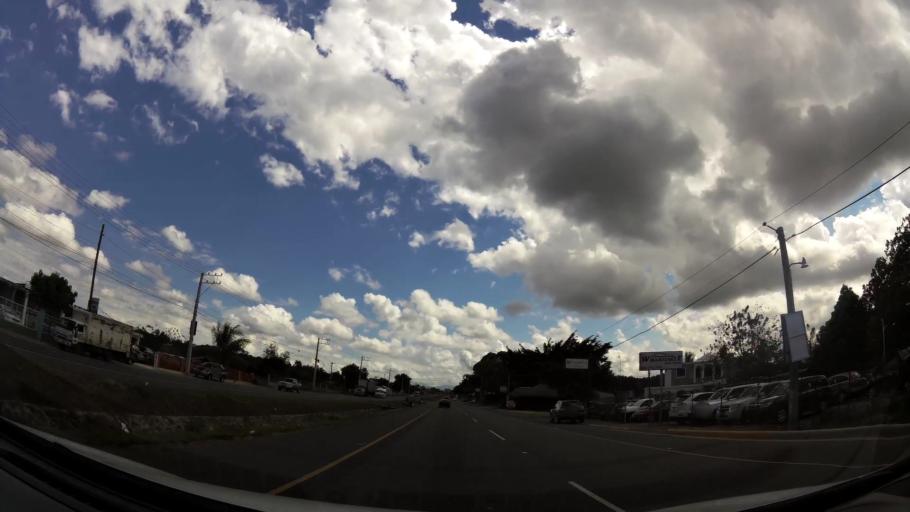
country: DO
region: La Vega
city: Rio Verde Arriba
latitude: 19.3612
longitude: -70.6022
